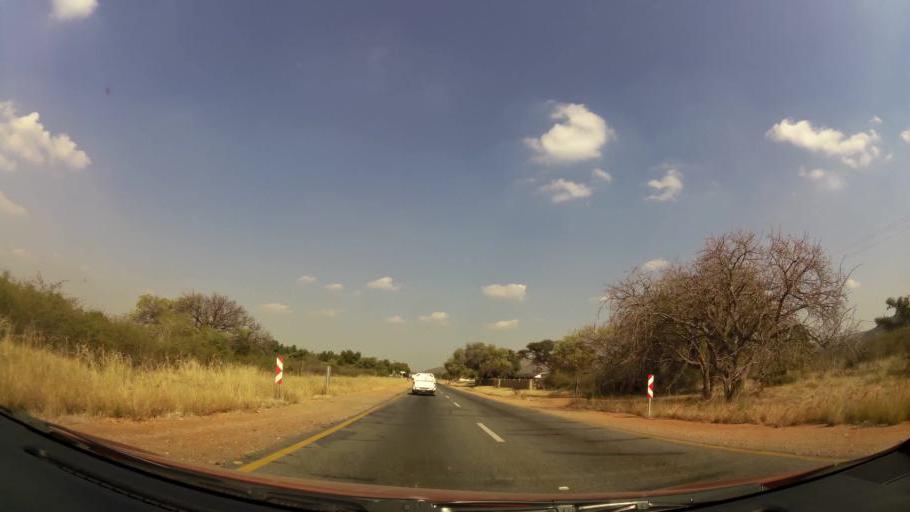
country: ZA
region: North-West
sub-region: Bojanala Platinum District Municipality
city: Rustenburg
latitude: -25.4836
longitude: 27.0863
